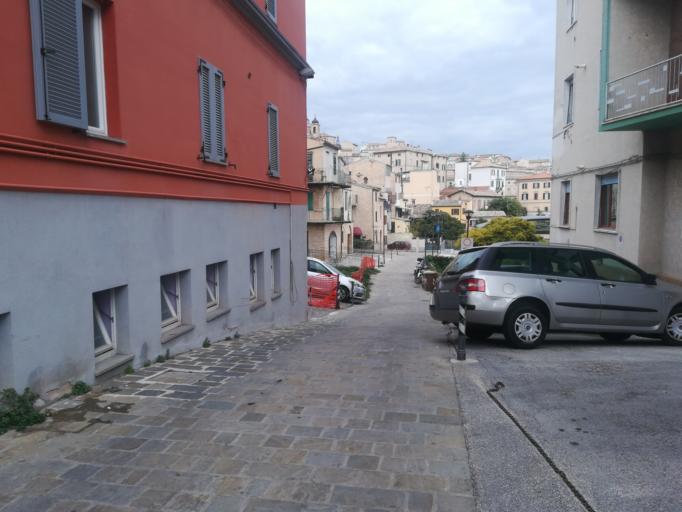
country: IT
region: The Marches
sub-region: Provincia di Macerata
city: Macerata
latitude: 43.2971
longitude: 13.4566
